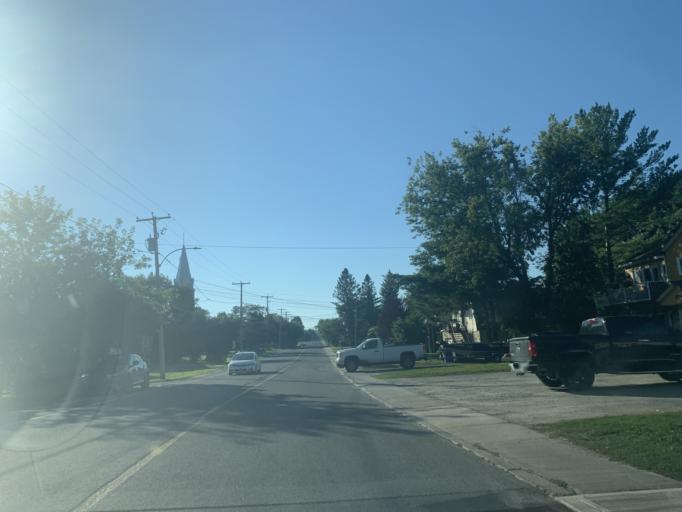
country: CA
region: Ontario
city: Hawkesbury
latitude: 45.6235
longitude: -74.5994
